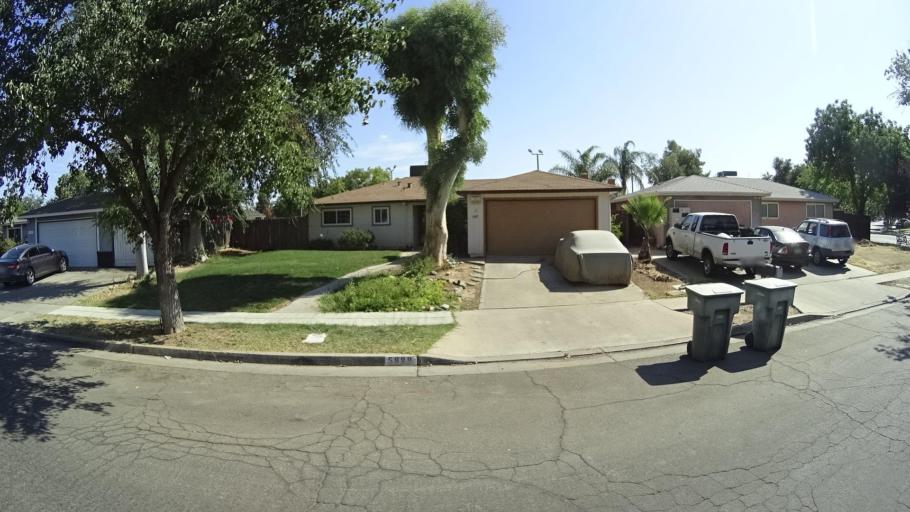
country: US
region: California
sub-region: Fresno County
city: Tarpey Village
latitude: 36.7890
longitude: -119.6874
